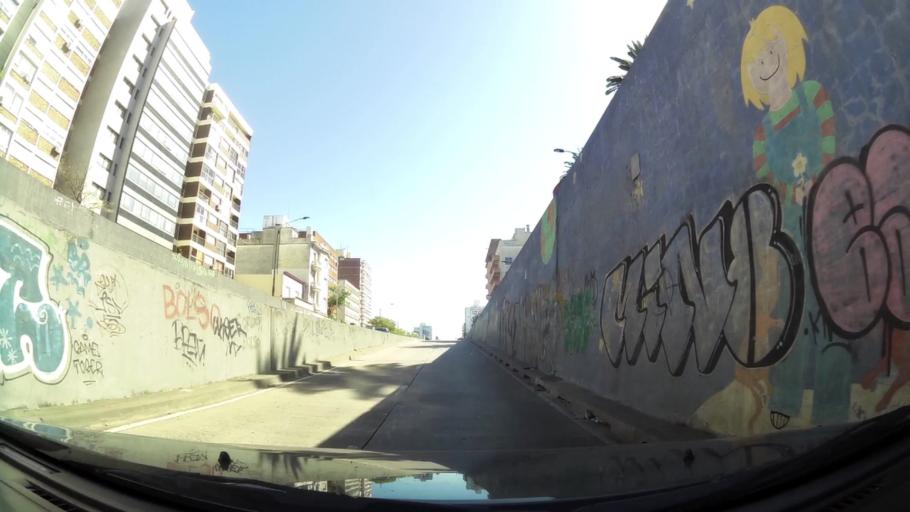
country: UY
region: Montevideo
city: Montevideo
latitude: -34.8937
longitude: -56.1637
